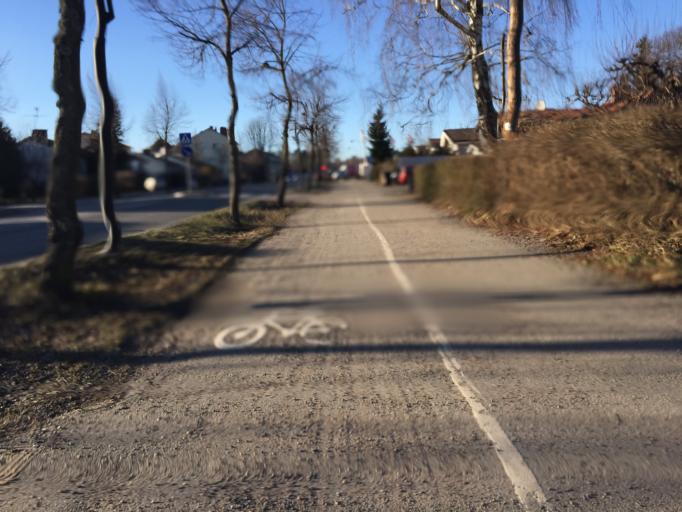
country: SE
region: Stockholm
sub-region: Stockholms Kommun
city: Bromma
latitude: 59.3555
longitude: 17.9127
